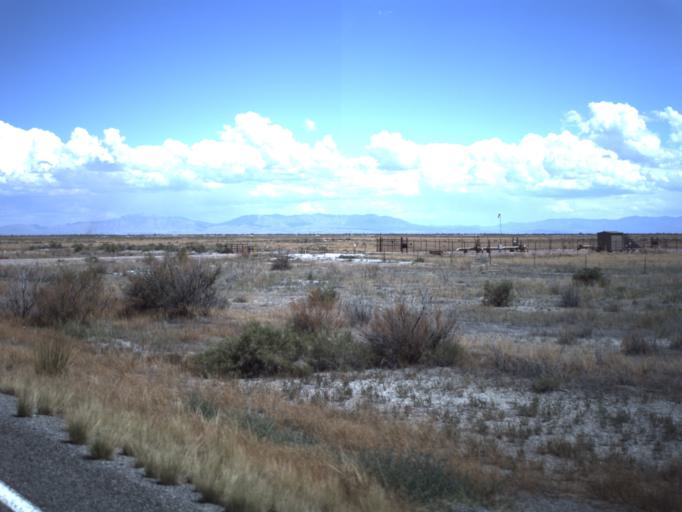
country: US
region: Utah
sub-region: Millard County
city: Delta
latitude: 39.2924
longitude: -112.8250
